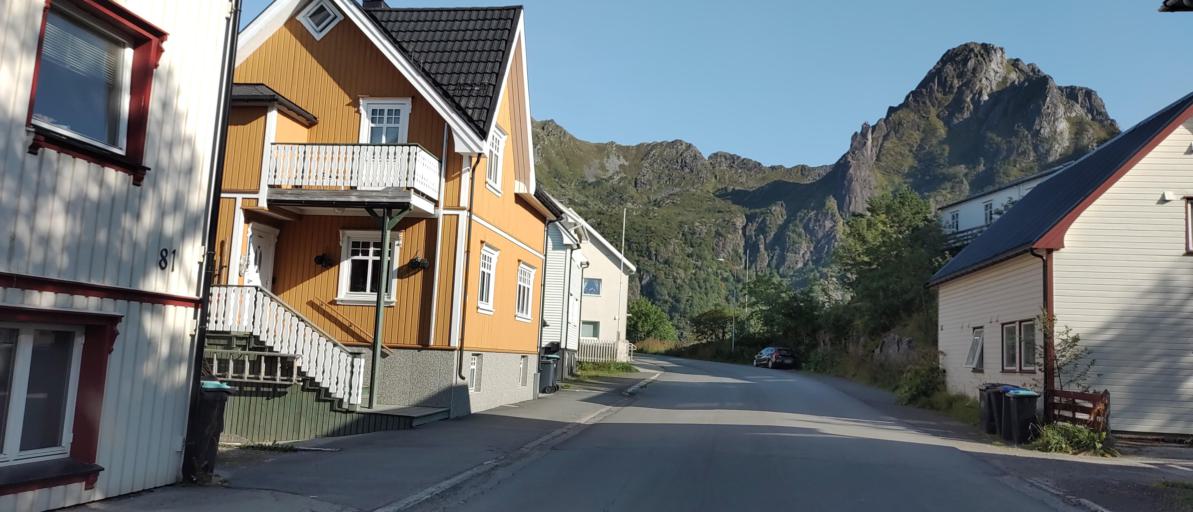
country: NO
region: Nordland
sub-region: Vagan
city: Svolvaer
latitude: 68.2369
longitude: 14.5708
